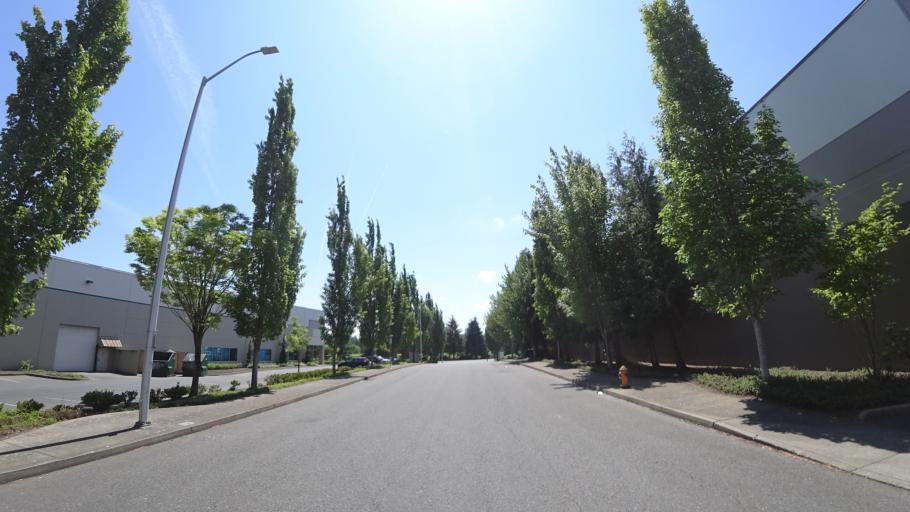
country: US
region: Oregon
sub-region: Multnomah County
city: Fairview
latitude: 45.5600
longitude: -122.5052
